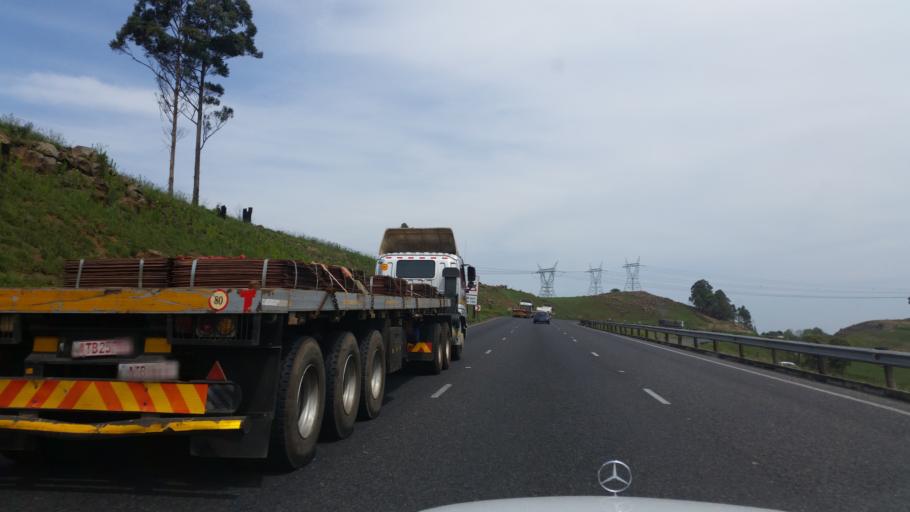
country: ZA
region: KwaZulu-Natal
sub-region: uMgungundlovu District Municipality
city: Howick
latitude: -29.4394
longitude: 30.1743
